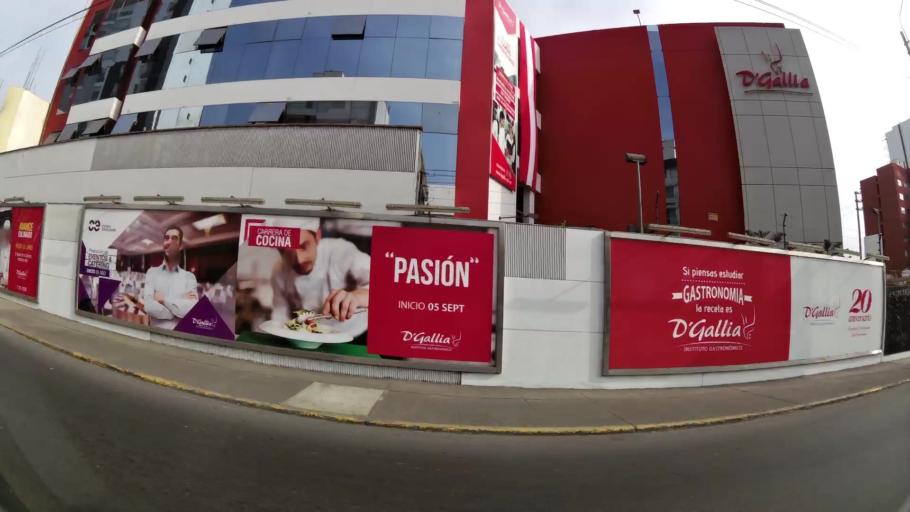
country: PE
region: Lima
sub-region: Lima
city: San Isidro
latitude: -12.0981
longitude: -77.0691
